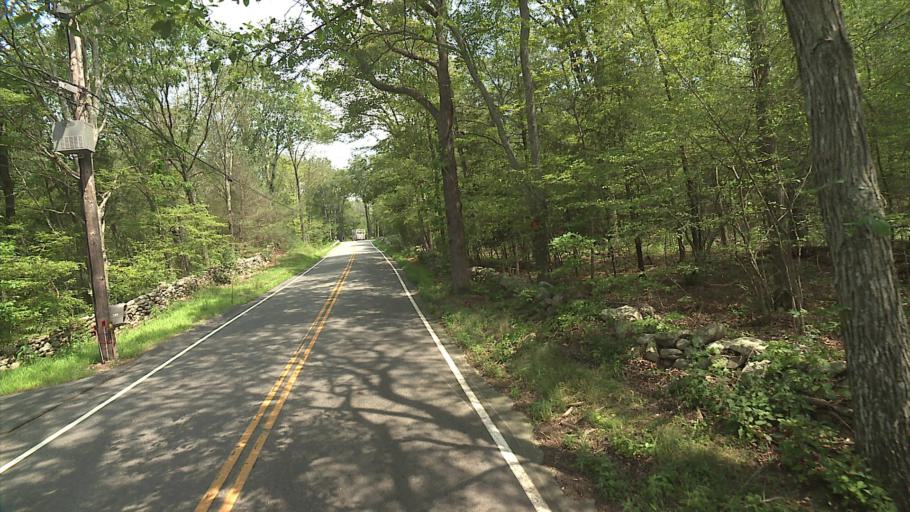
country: US
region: Connecticut
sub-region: Windham County
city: Danielson
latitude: 41.7664
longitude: -71.8463
